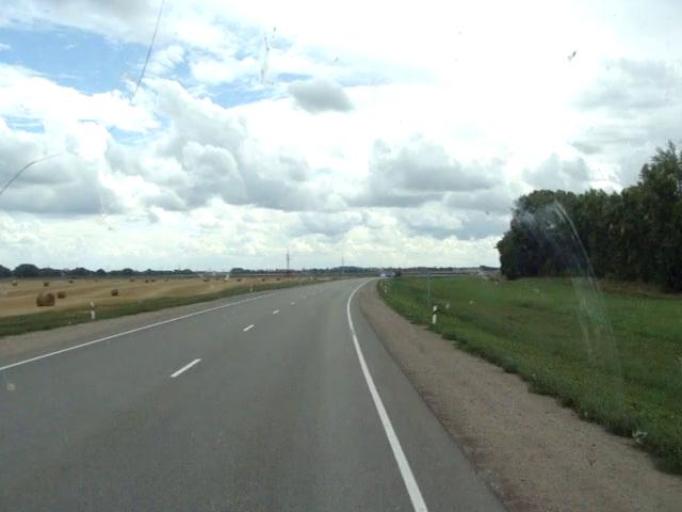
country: RU
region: Altai Krai
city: Shubenka
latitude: 52.6819
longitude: 85.0468
